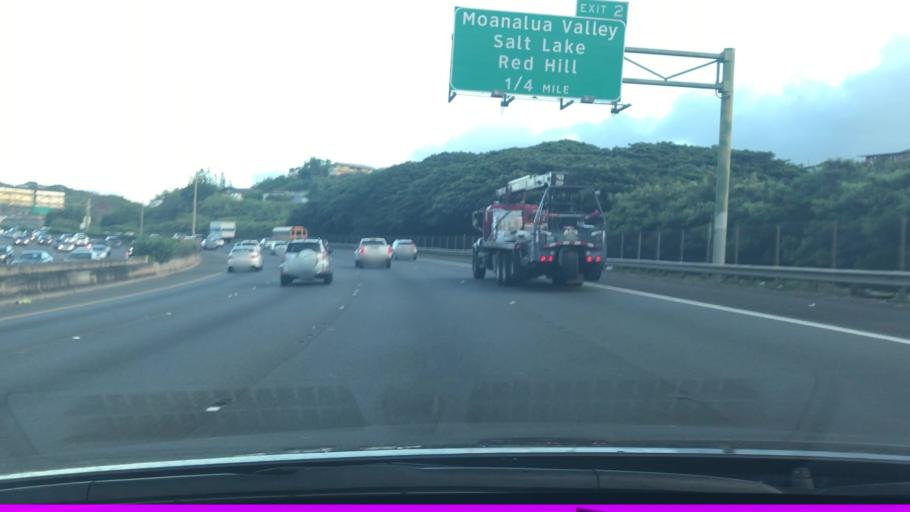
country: US
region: Hawaii
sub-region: Honolulu County
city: Halawa Heights
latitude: 21.3533
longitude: -157.8963
